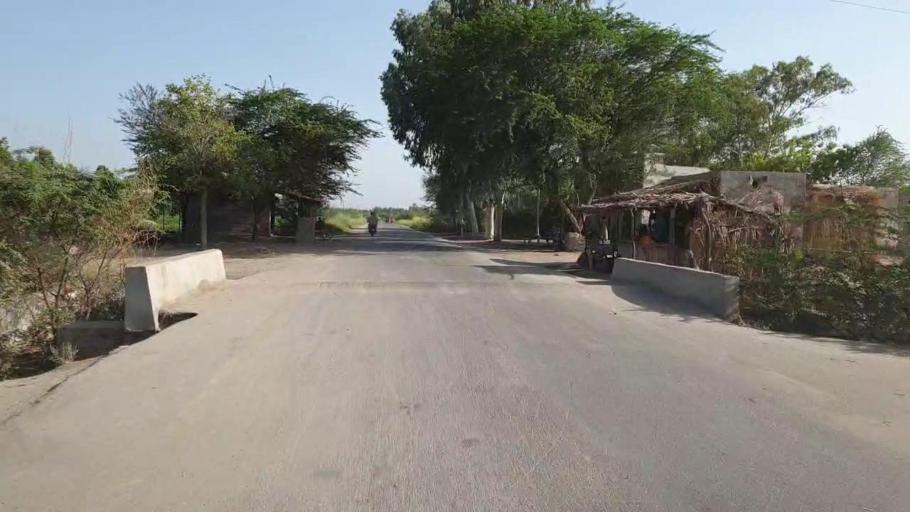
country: PK
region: Sindh
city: Daur
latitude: 26.4617
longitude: 68.4512
